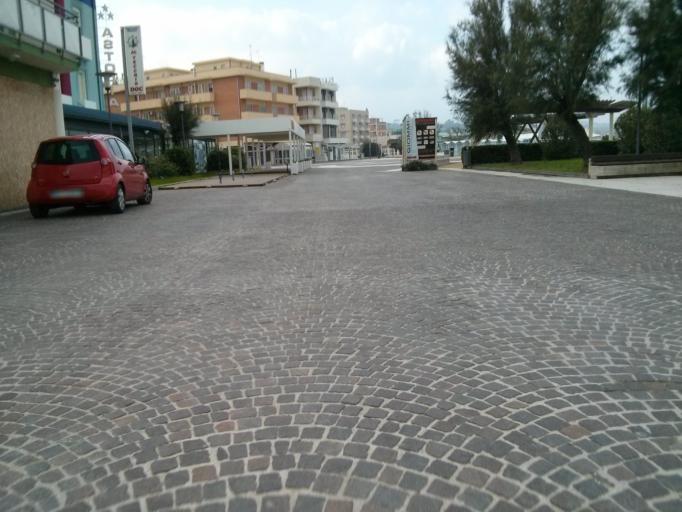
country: IT
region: The Marches
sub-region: Provincia di Pesaro e Urbino
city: Fano
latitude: 43.8508
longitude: 13.0141
